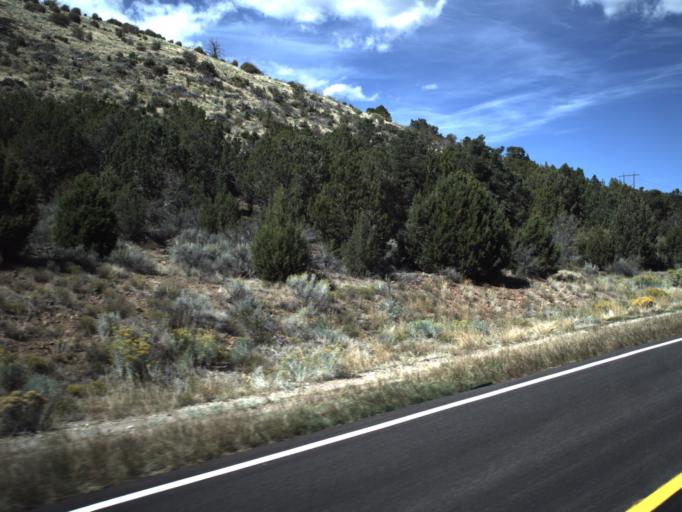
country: US
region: Utah
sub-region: Washington County
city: Enterprise
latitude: 37.4284
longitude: -113.6292
